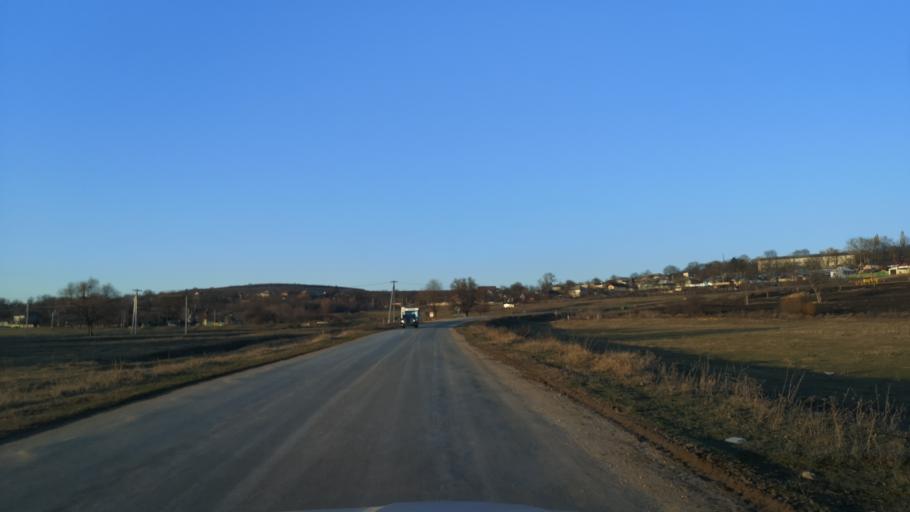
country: MD
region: Orhei
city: Orhei
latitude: 47.3523
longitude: 28.6950
